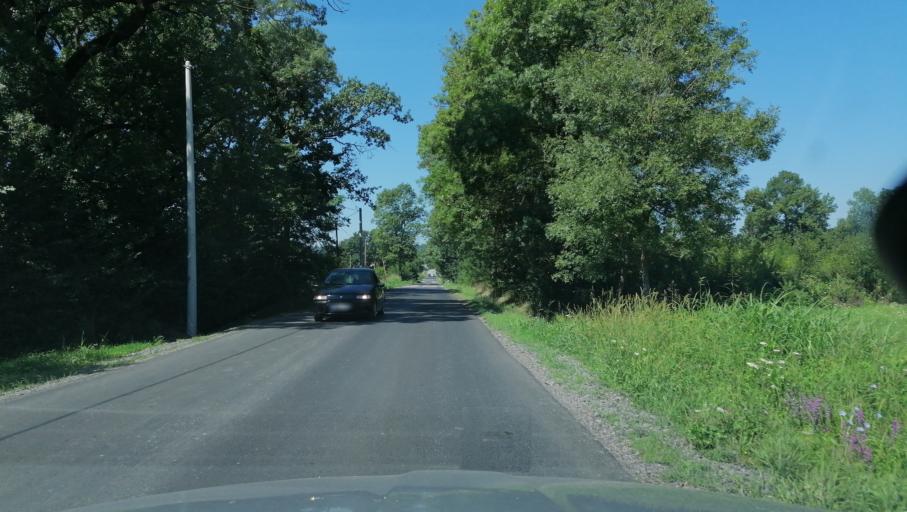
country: RS
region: Central Serbia
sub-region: Raski Okrug
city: Vrnjacka Banja
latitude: 43.7169
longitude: 20.8127
